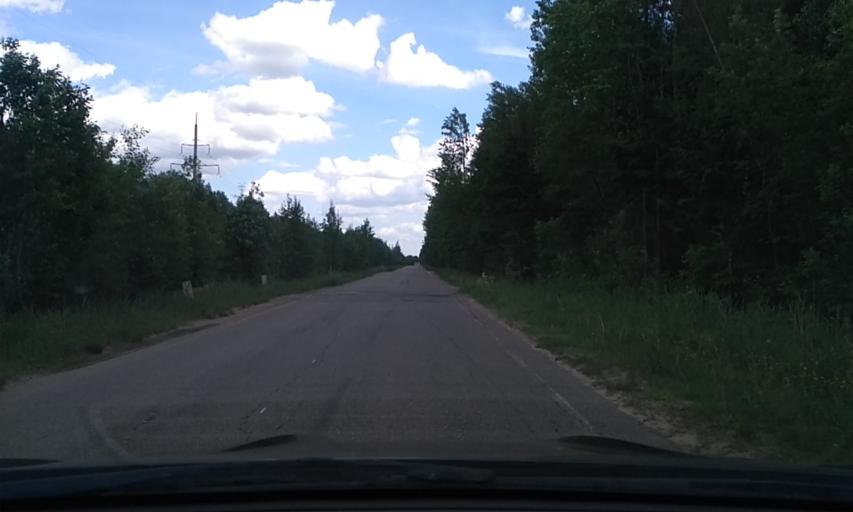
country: RU
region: Leningrad
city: Otradnoye
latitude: 59.8202
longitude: 30.8029
